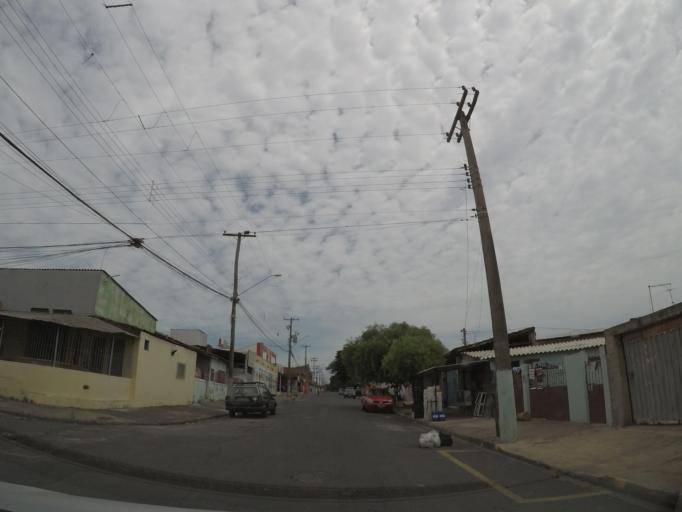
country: BR
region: Sao Paulo
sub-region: Hortolandia
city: Hortolandia
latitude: -22.8384
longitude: -47.1900
